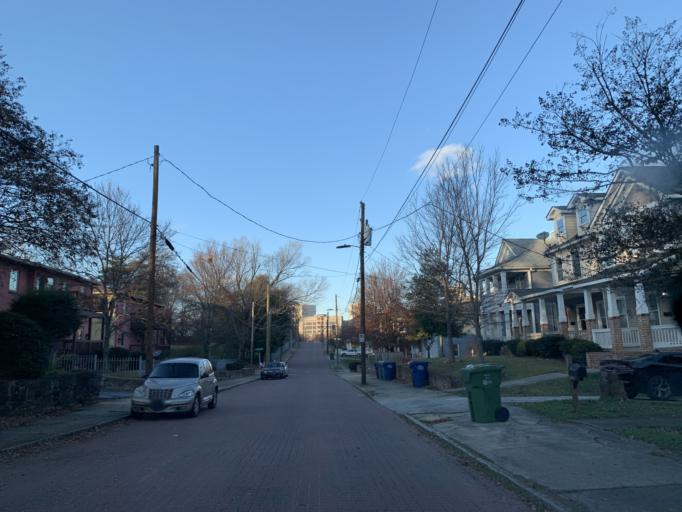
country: US
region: Georgia
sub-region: Fulton County
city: Atlanta
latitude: 33.7388
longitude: -84.3958
